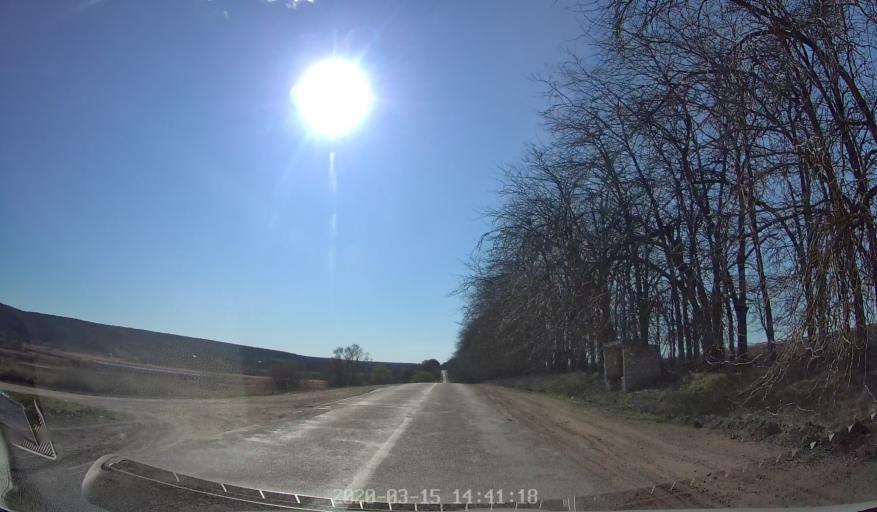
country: MD
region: Orhei
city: Orhei
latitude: 47.2923
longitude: 28.8915
